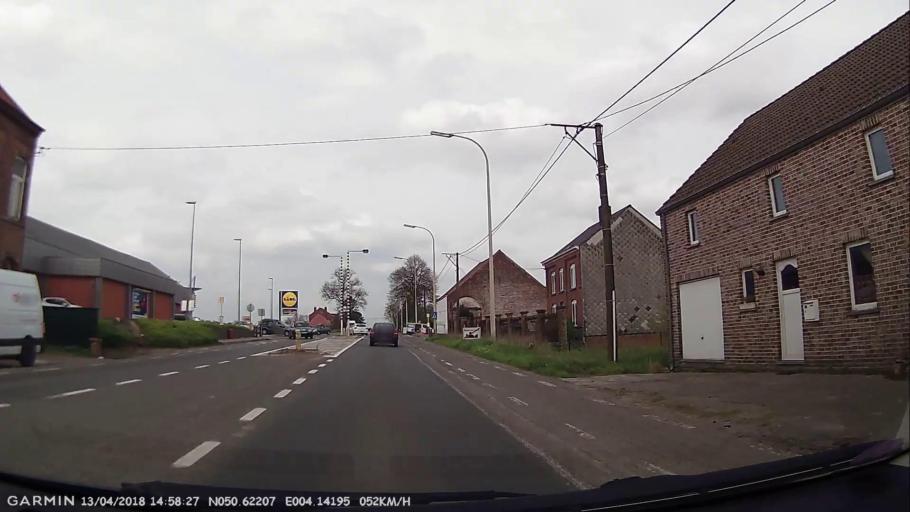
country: BE
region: Wallonia
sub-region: Province du Hainaut
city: Braine-le-Comte
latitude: 50.6222
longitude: 4.1421
